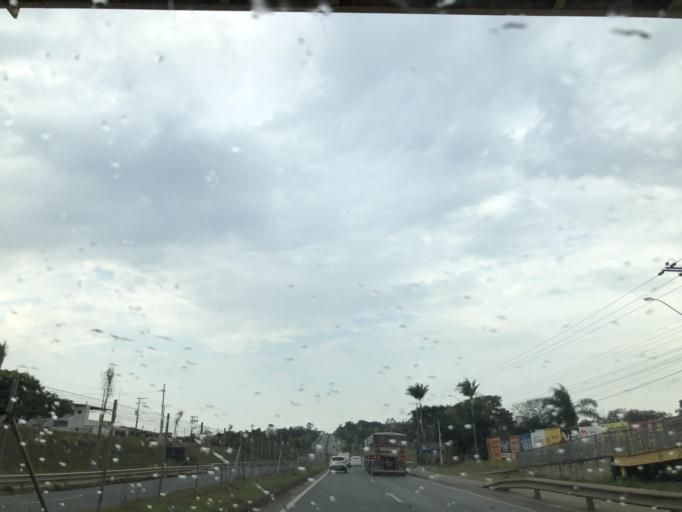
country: BR
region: Sao Paulo
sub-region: Salto De Pirapora
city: Salto de Pirapora
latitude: -23.6387
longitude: -47.5739
